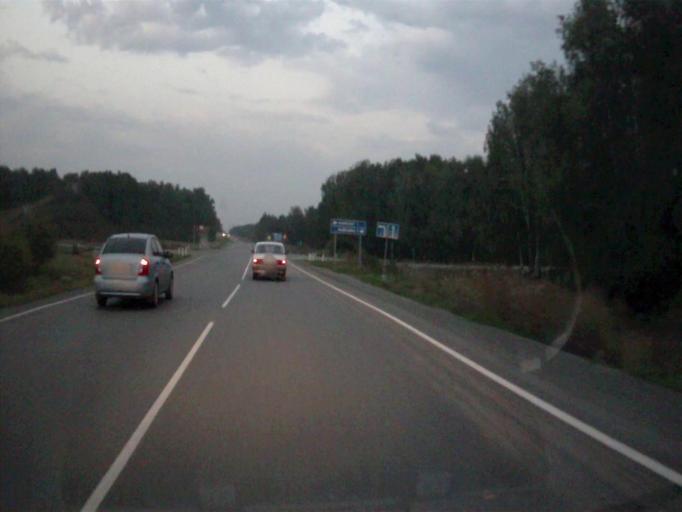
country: RU
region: Chelyabinsk
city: Timiryazevskiy
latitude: 55.2046
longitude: 60.7680
